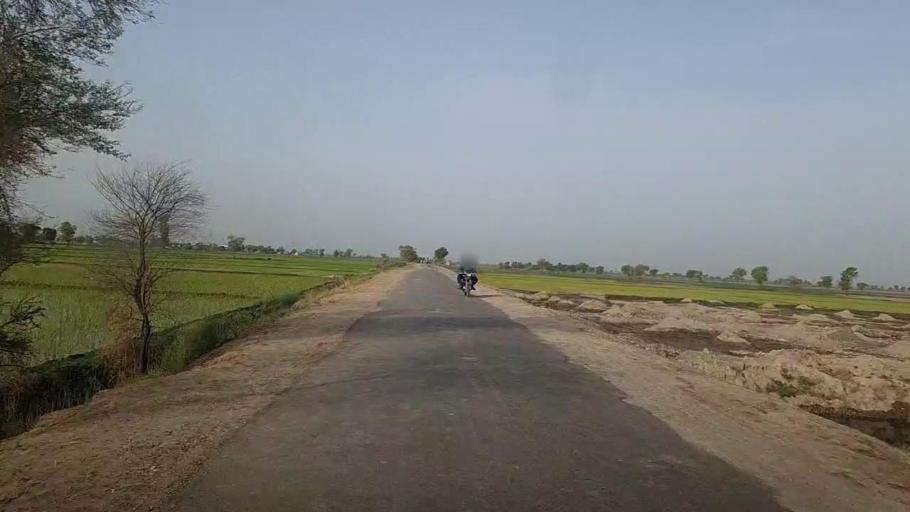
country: PK
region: Sindh
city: Mehar
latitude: 27.1610
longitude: 67.8105
